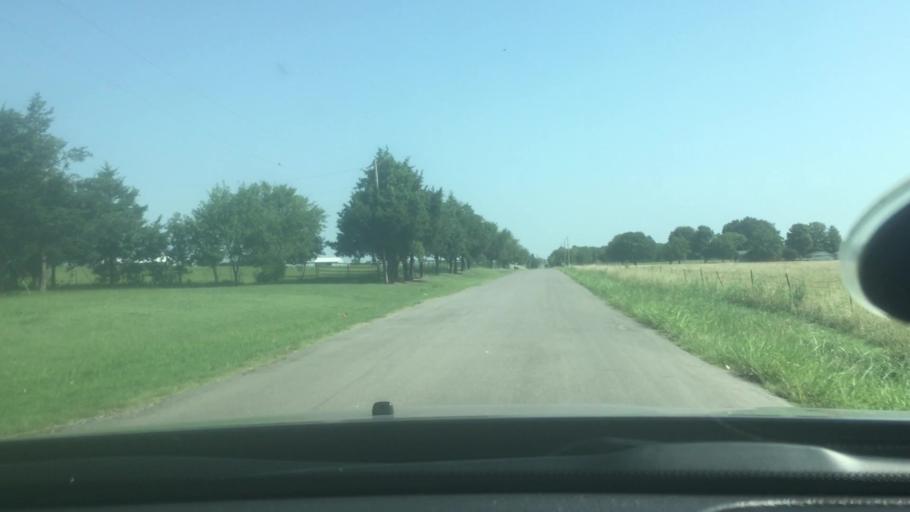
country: US
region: Oklahoma
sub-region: Bryan County
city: Calera
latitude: 33.9885
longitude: -96.4656
